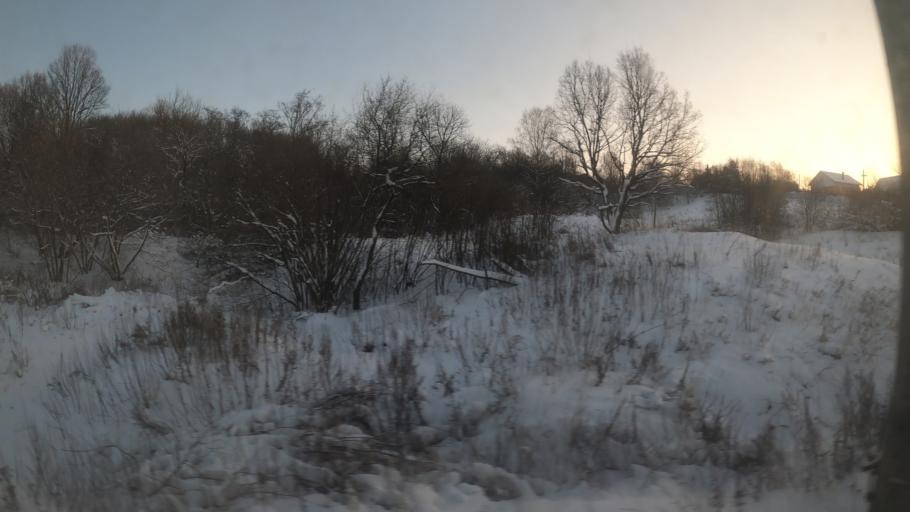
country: RU
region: Moskovskaya
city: Dedenevo
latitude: 56.2747
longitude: 37.5073
